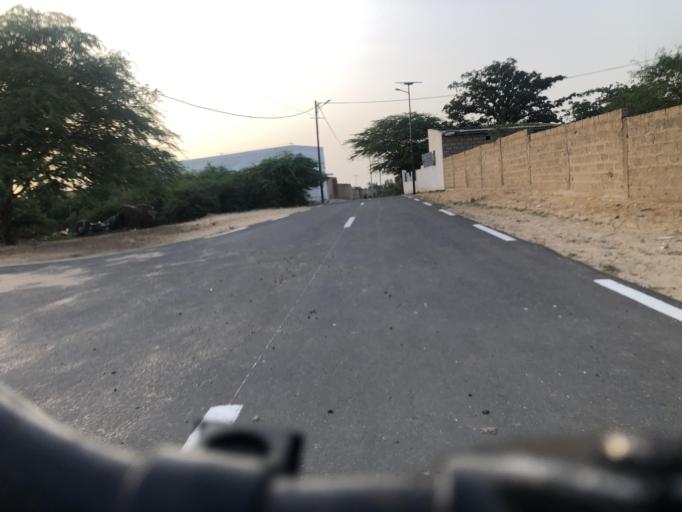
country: SN
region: Saint-Louis
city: Saint-Louis
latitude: 16.0692
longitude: -16.4275
